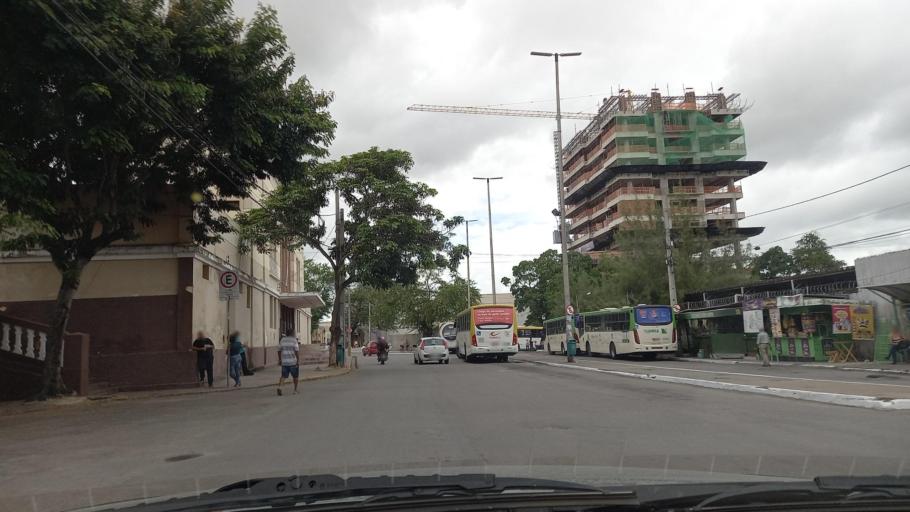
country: BR
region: Pernambuco
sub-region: Caruaru
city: Caruaru
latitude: -8.2831
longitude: -35.9699
